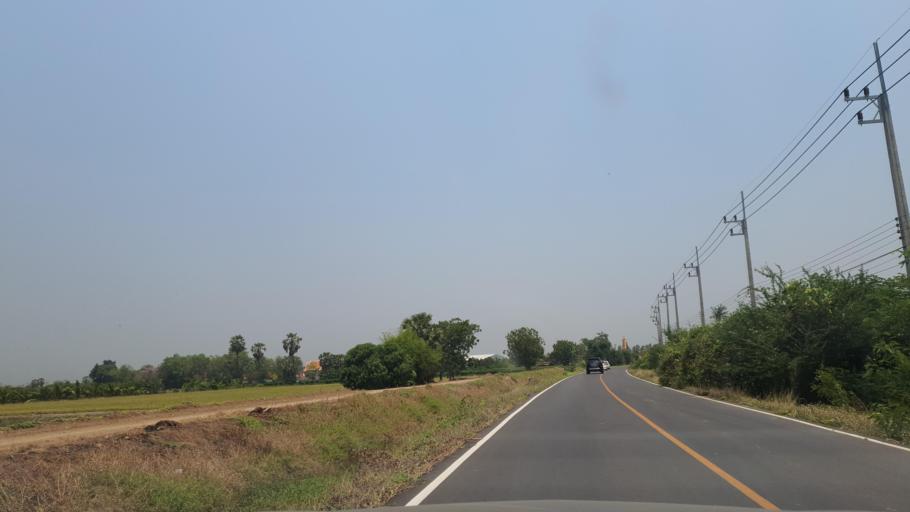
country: TH
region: Suphan Buri
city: Si Prachan
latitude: 14.5984
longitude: 100.1018
